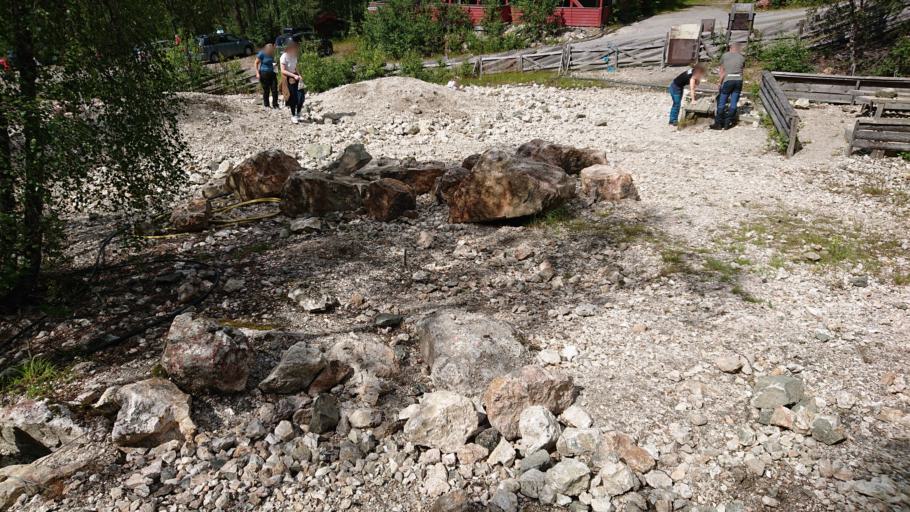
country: NO
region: Aust-Agder
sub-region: Evje og Hornnes
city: Evje
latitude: 58.5977
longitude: 7.8563
